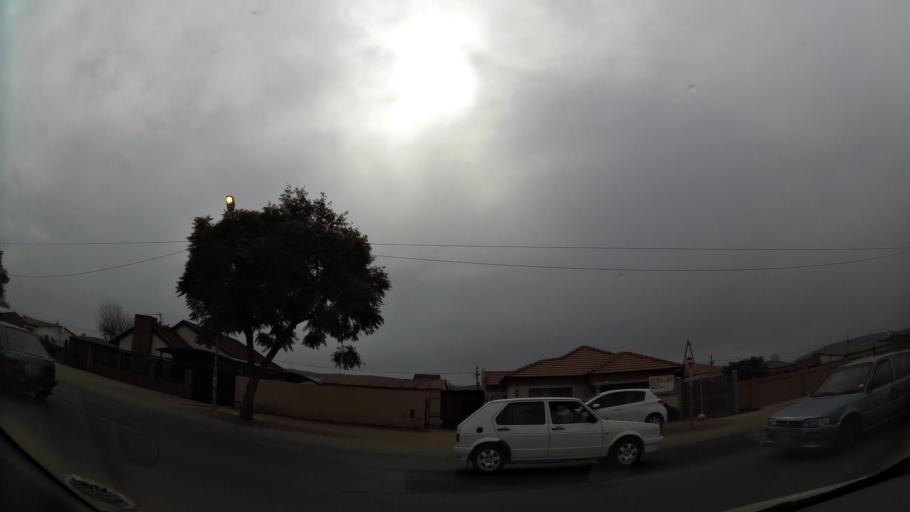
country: ZA
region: Gauteng
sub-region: City of Tshwane Metropolitan Municipality
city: Pretoria
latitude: -25.7148
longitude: 28.3432
